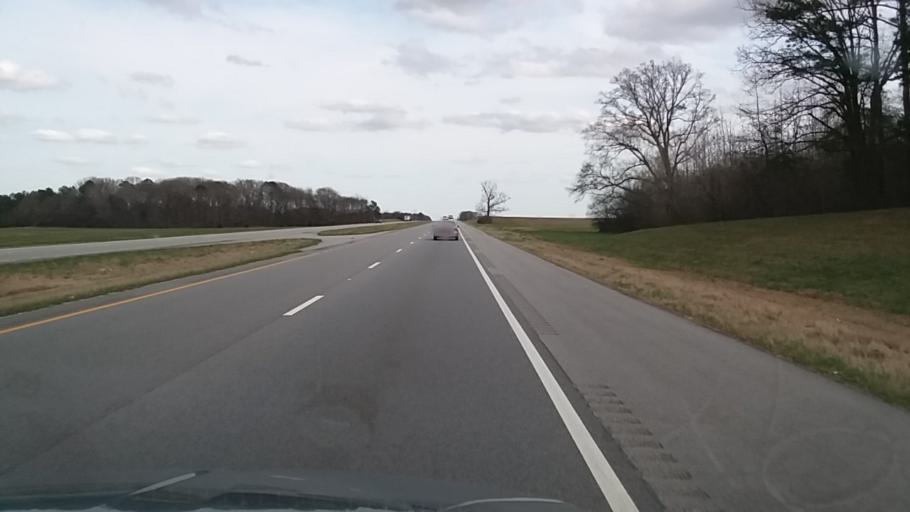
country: US
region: Alabama
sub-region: Lawrence County
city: Town Creek
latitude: 34.6828
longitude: -87.4812
